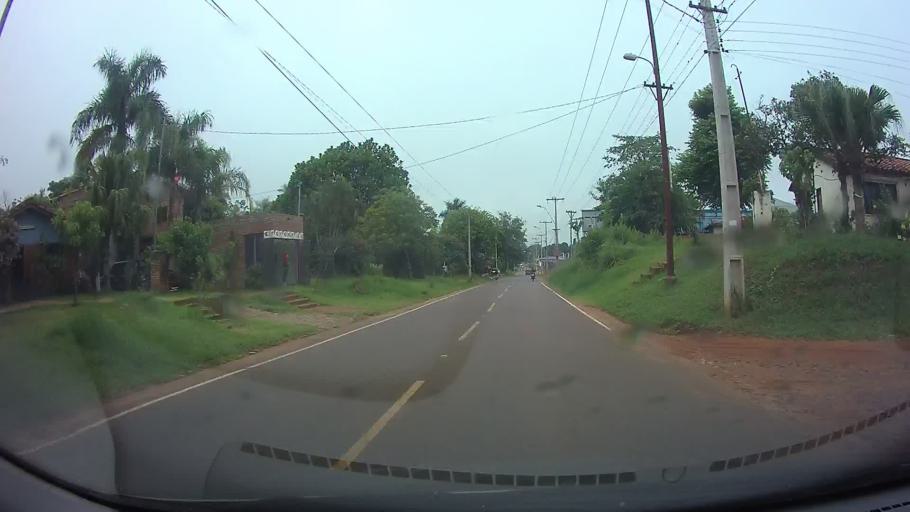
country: PY
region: Central
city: Itaugua
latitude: -25.3785
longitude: -57.3494
